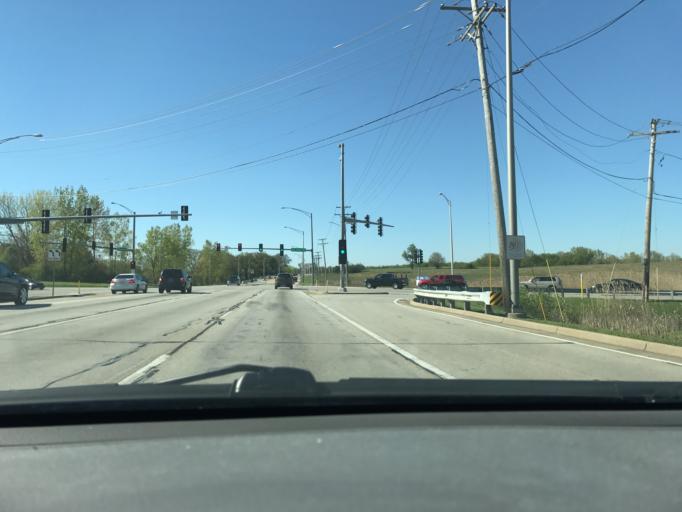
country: US
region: Illinois
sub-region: Kane County
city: Sleepy Hollow
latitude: 42.0657
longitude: -88.3357
